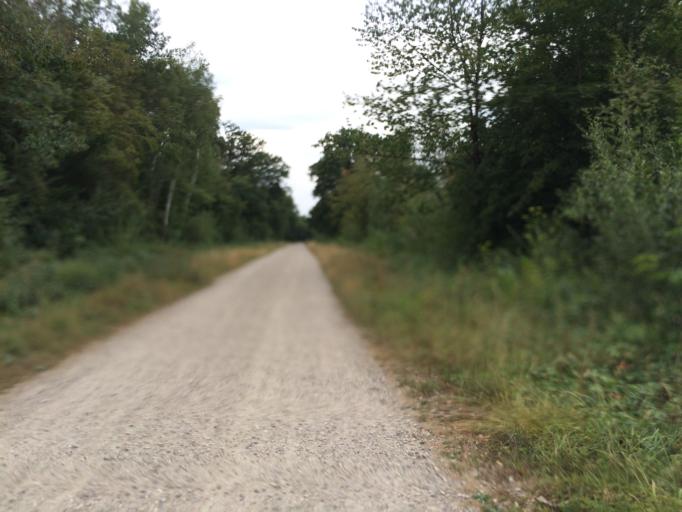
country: FR
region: Ile-de-France
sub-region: Departement de Seine-et-Marne
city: Lieusaint
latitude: 48.6497
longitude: 2.5366
